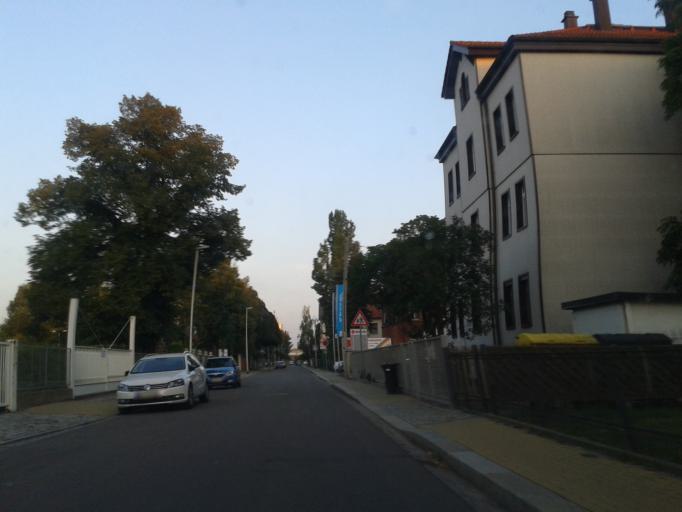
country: DE
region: Saxony
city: Radebeul
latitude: 51.0962
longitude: 13.6823
